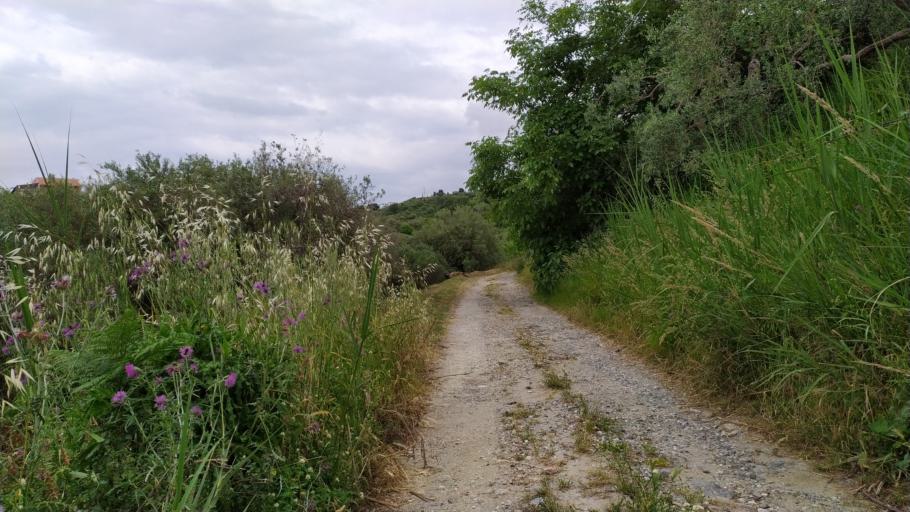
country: IT
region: Sicily
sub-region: Messina
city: Gualtieri Sicamino
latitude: 38.1564
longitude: 15.2989
